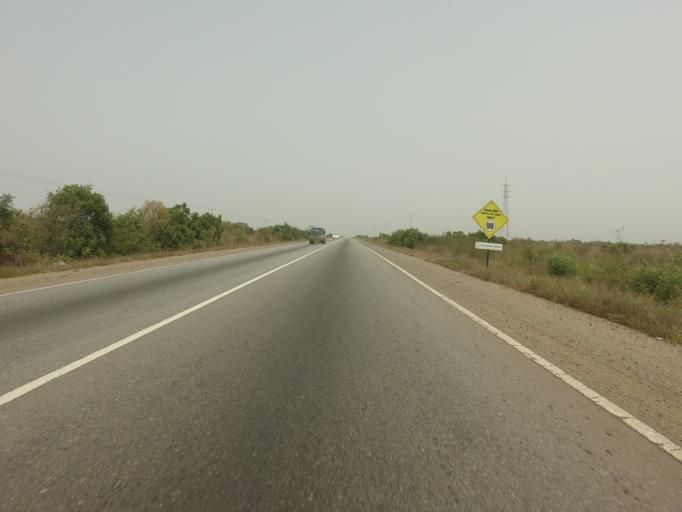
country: GH
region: Greater Accra
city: Tema
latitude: 5.7900
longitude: 0.1145
